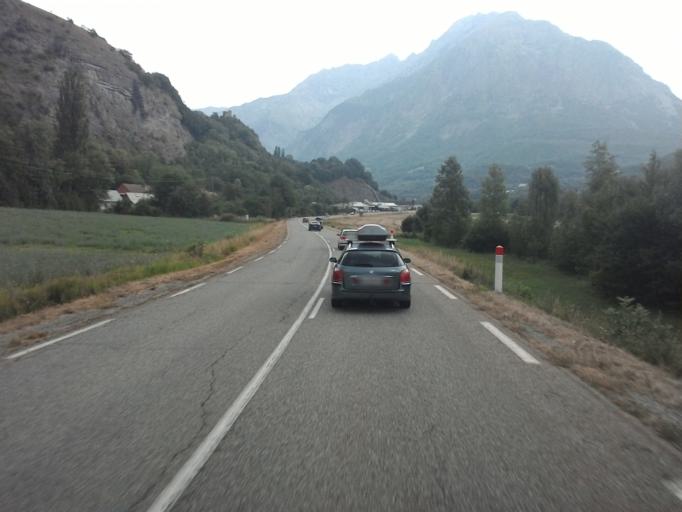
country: FR
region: Provence-Alpes-Cote d'Azur
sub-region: Departement des Hautes-Alpes
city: Saint-Bonnet-en-Champsaur
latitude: 44.7773
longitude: 6.0079
